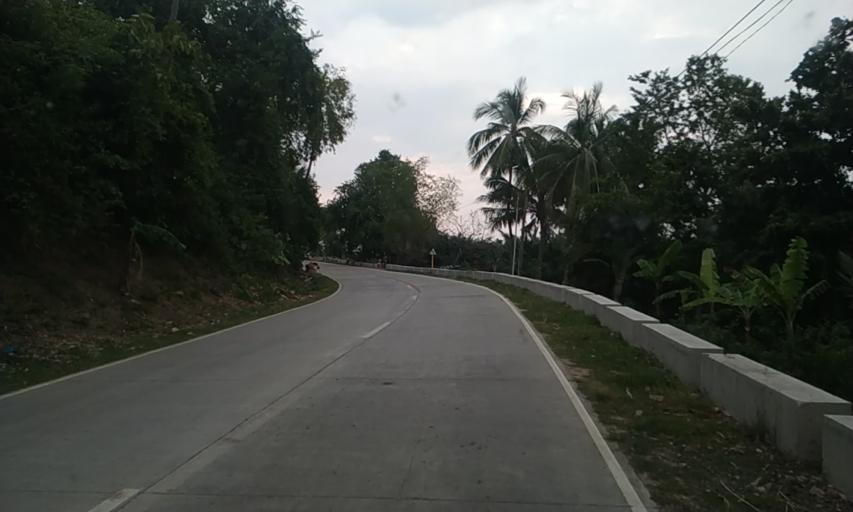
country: PH
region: Central Visayas
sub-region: Province of Negros Oriental
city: Calamba
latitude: 10.1972
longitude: 123.2964
